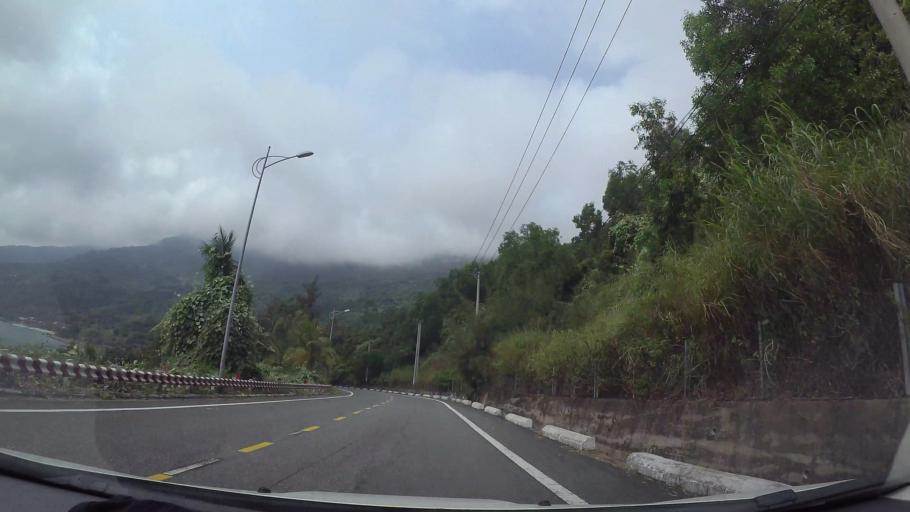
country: VN
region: Da Nang
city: Son Tra
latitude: 16.1032
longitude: 108.3019
